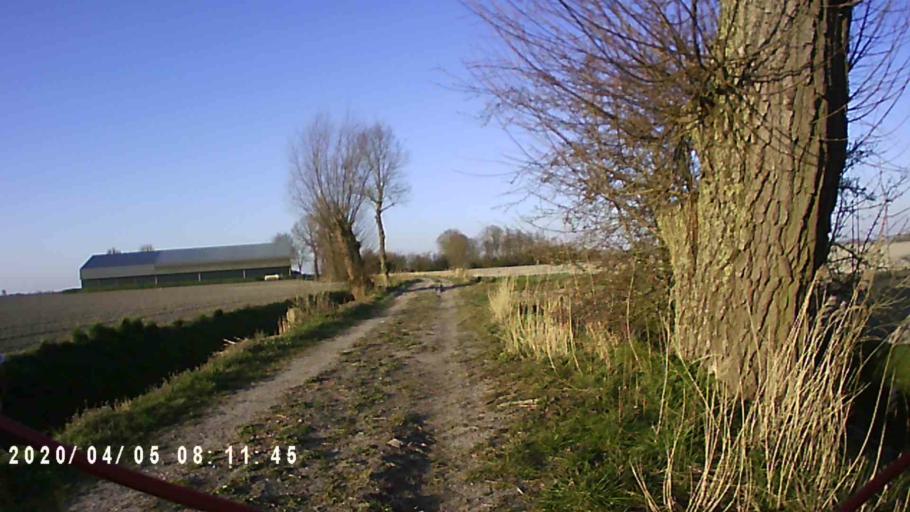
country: NL
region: Groningen
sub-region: Gemeente Zuidhorn
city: Oldehove
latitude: 53.3472
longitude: 6.4452
